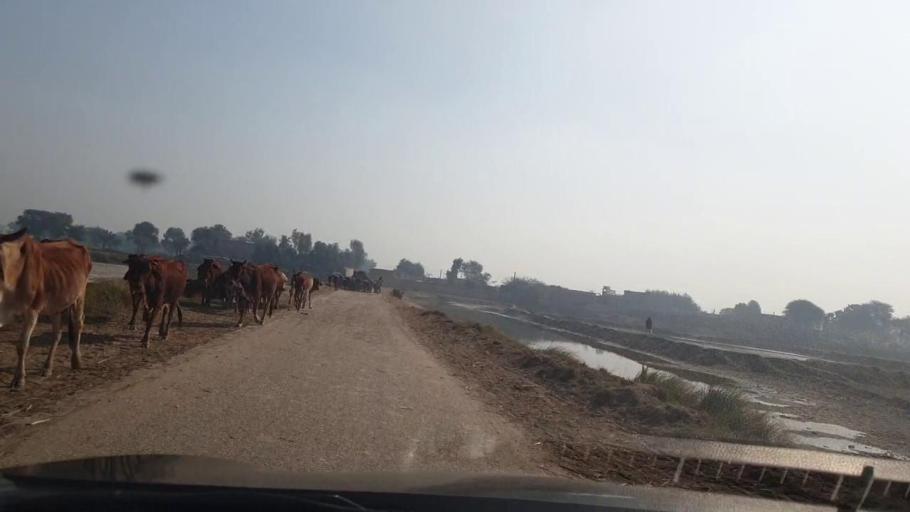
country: PK
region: Sindh
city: Ubauro
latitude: 28.1160
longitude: 69.7228
